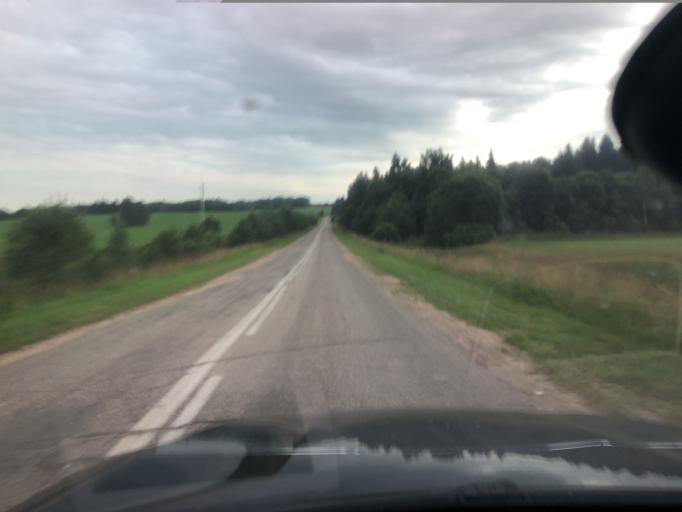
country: RU
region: Jaroslavl
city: Pereslavl'-Zalesskiy
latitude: 57.0215
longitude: 38.9456
